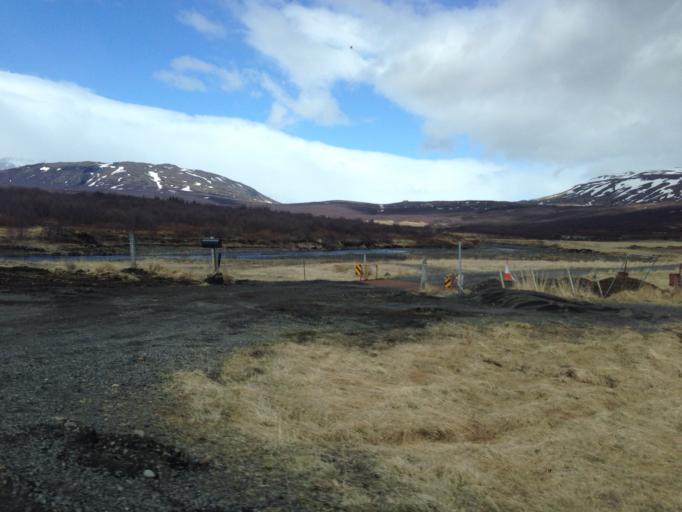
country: IS
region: South
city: Selfoss
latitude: 64.2769
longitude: -20.4231
